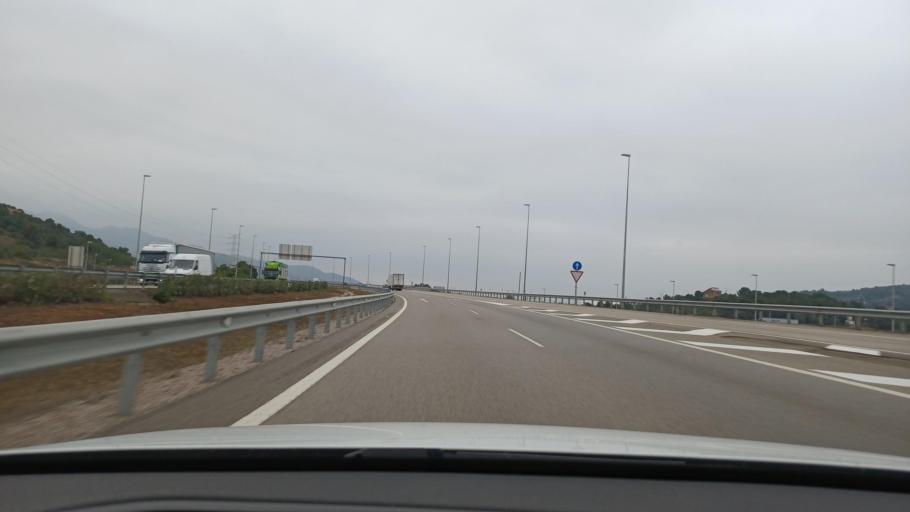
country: ES
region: Valencia
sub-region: Provincia de Castello
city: Chilches
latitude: 39.7949
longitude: -0.2239
